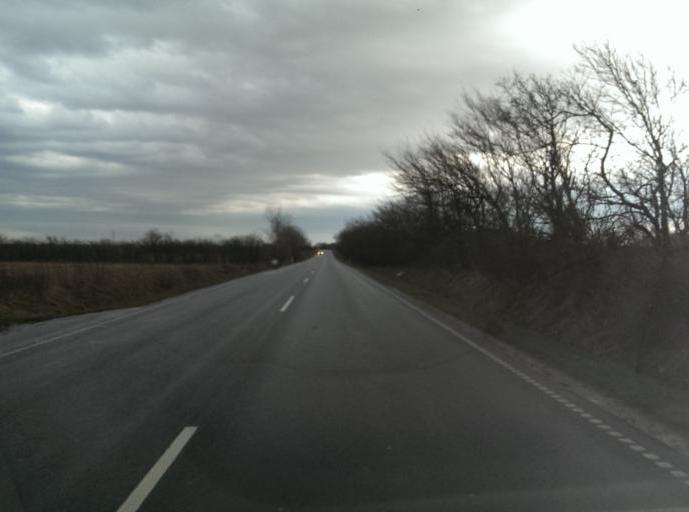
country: DK
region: South Denmark
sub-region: Esbjerg Kommune
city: Tjaereborg
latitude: 55.5129
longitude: 8.5939
